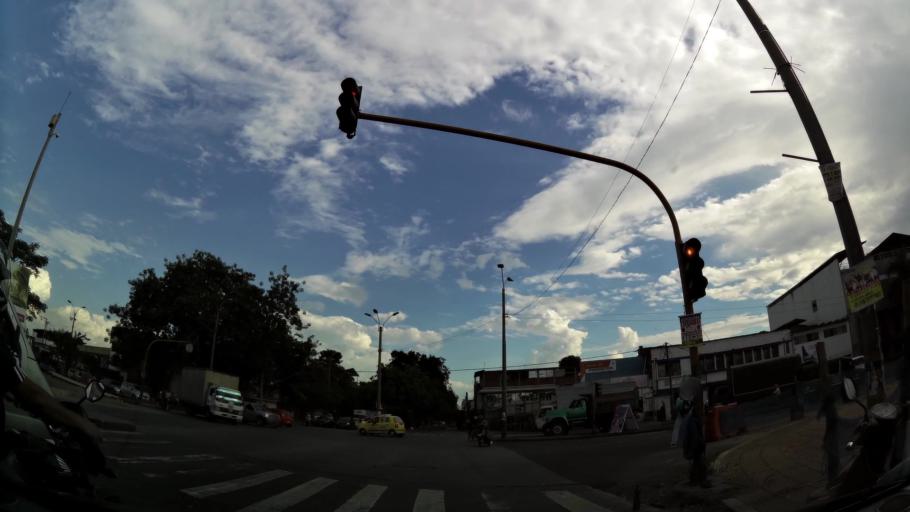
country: CO
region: Valle del Cauca
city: Cali
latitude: 3.4535
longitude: -76.5054
